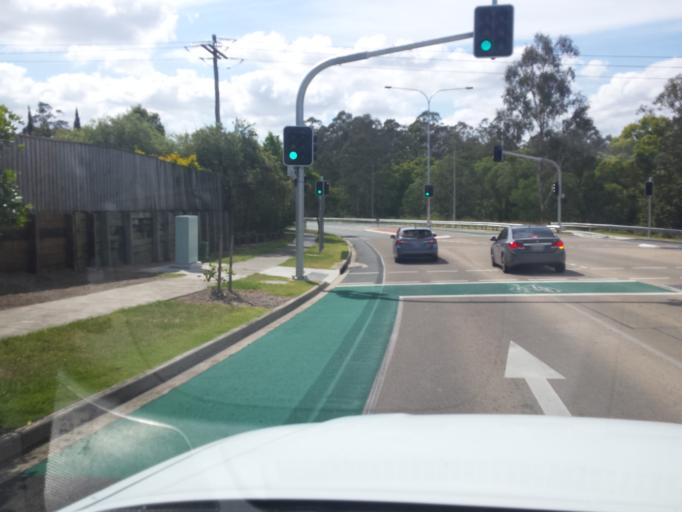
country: AU
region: Queensland
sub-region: Moreton Bay
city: Ferny Hills
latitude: -27.3835
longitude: 152.9624
